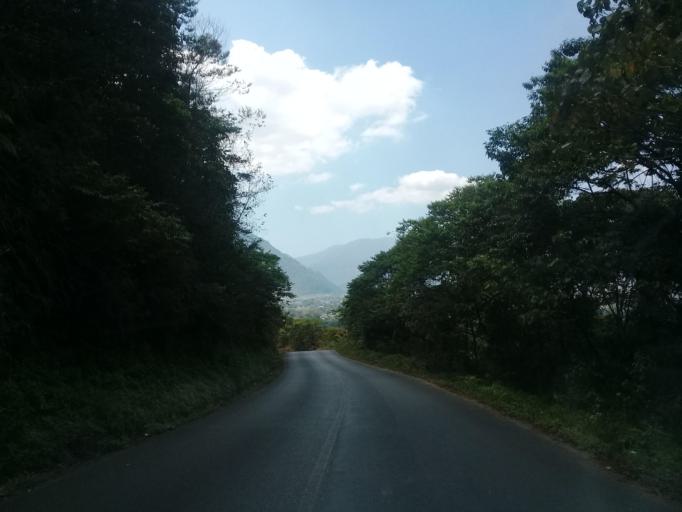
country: MX
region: Veracruz
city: Jalapilla
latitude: 18.8134
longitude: -97.0602
